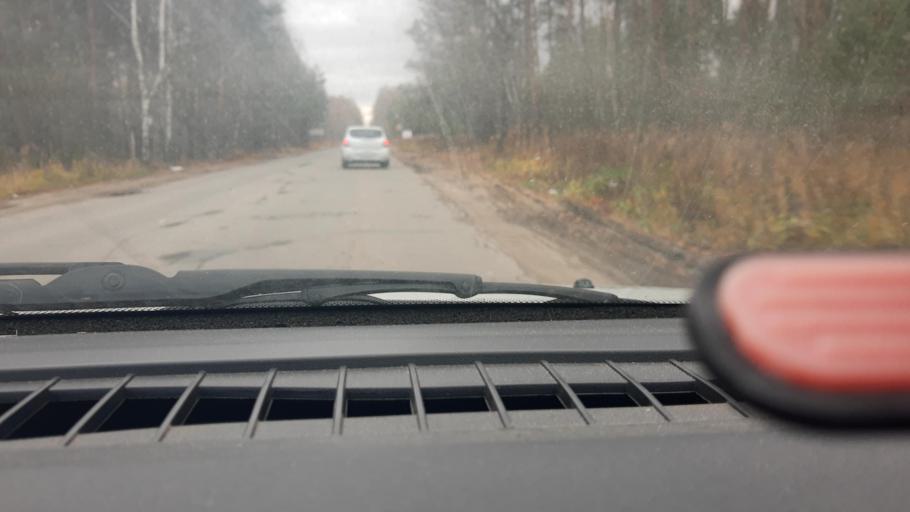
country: RU
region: Nizjnij Novgorod
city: Babino
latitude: 56.3026
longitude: 43.6635
